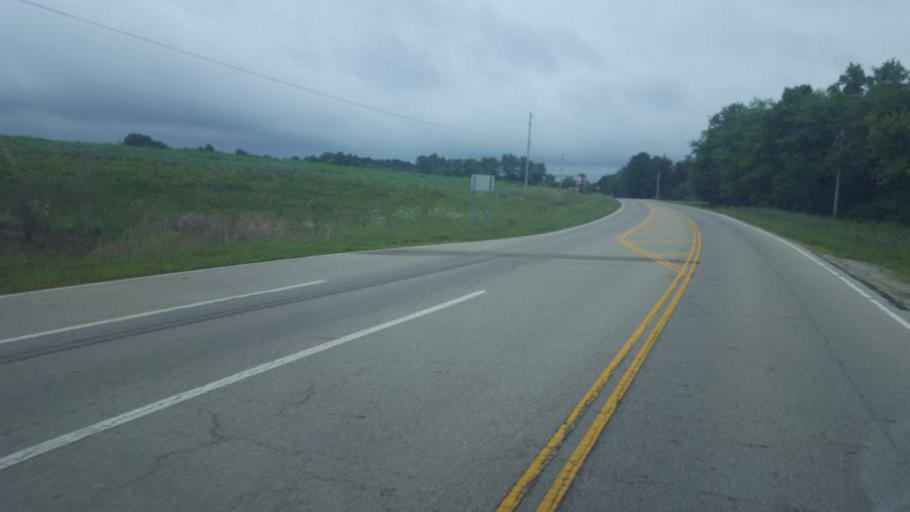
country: US
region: Ohio
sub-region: Delaware County
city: Sunbury
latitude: 40.3046
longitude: -82.8648
